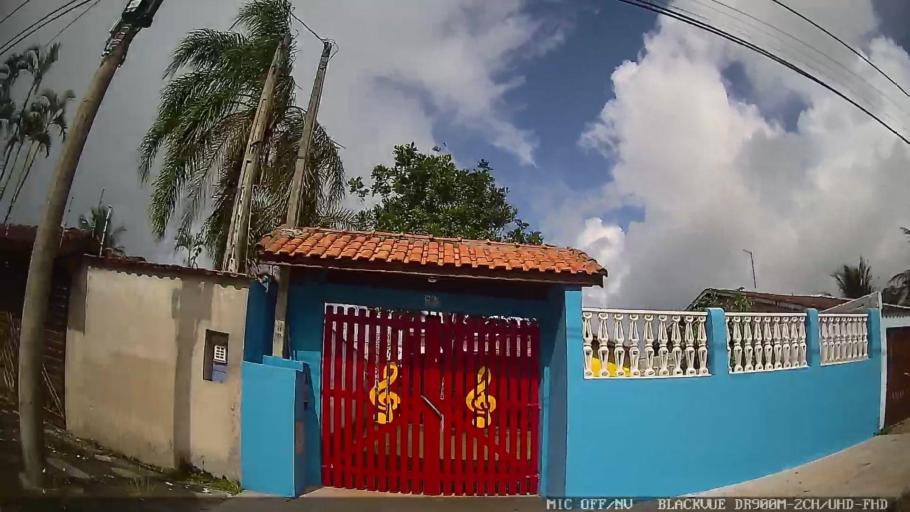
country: BR
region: Sao Paulo
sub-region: Itanhaem
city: Itanhaem
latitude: -24.2401
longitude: -46.8889
